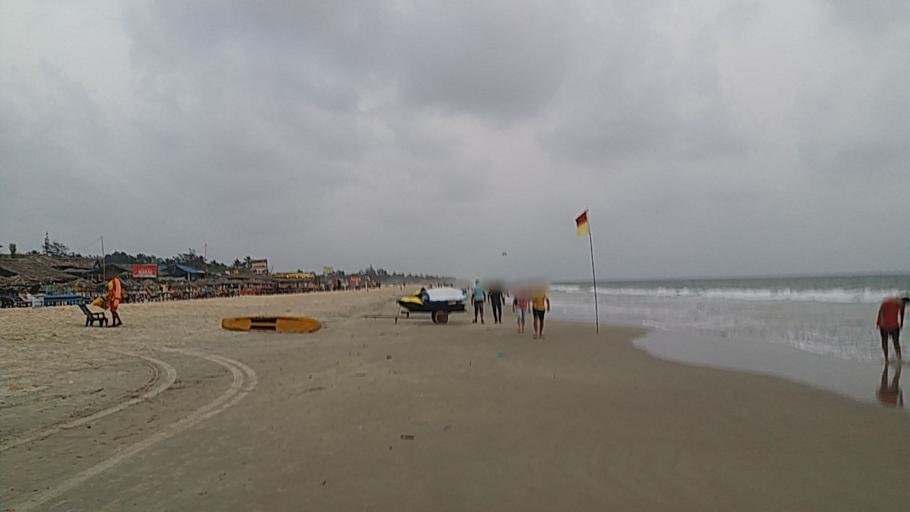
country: IN
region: Goa
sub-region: South Goa
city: Benaulim
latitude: 15.2559
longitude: 73.9190
